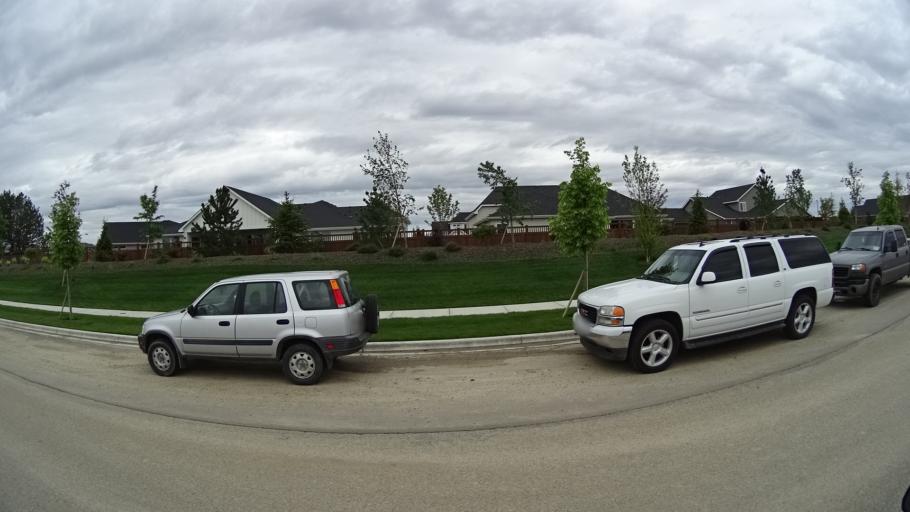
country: US
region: Idaho
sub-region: Ada County
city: Eagle
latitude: 43.7141
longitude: -116.4235
